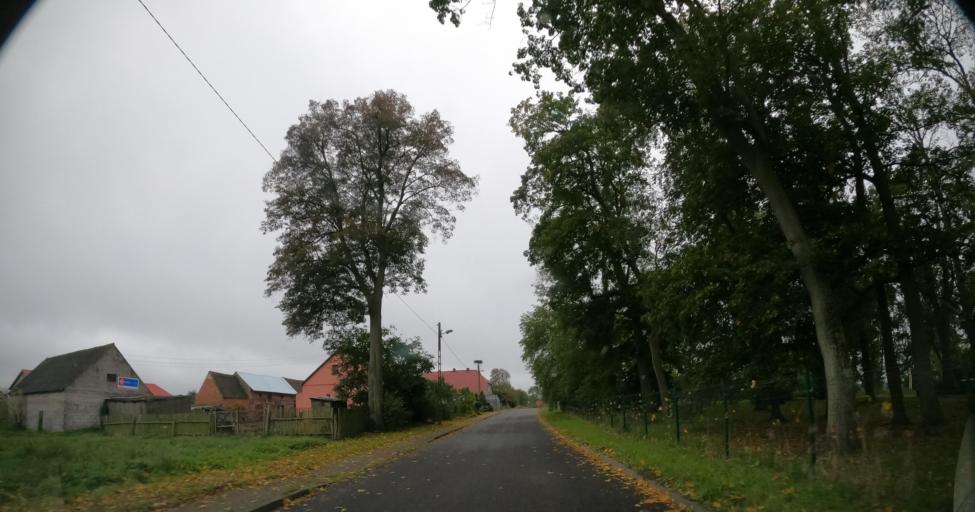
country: PL
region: West Pomeranian Voivodeship
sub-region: Powiat pyrzycki
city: Kozielice
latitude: 53.0951
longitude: 14.7681
